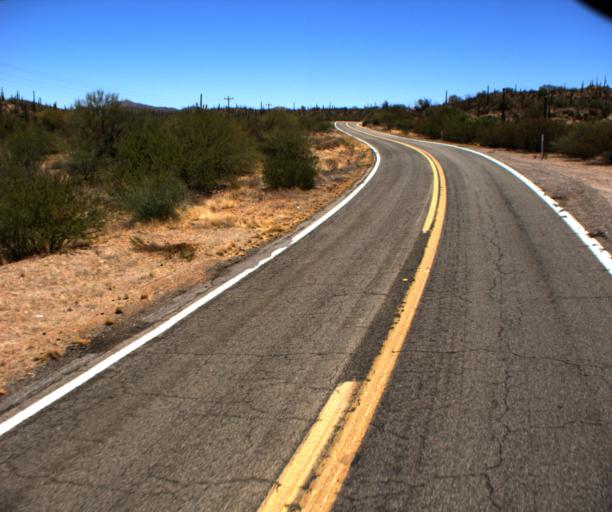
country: US
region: Arizona
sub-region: Pima County
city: Sells
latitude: 32.1732
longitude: -112.2159
